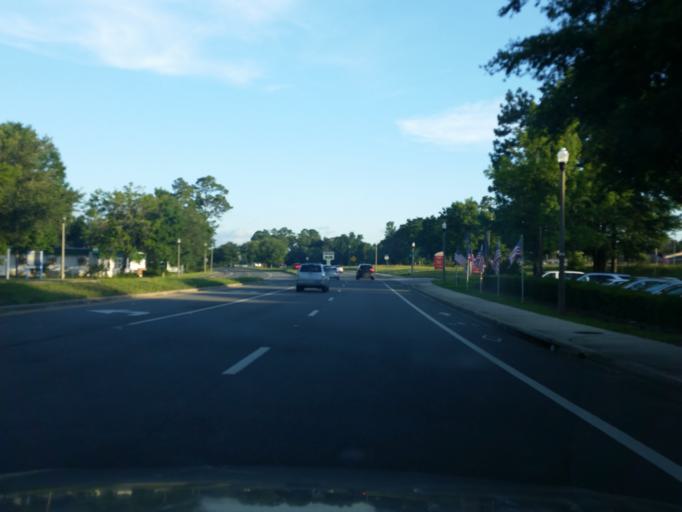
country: US
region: Florida
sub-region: Escambia County
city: Ferry Pass
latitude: 30.5249
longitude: -87.2214
